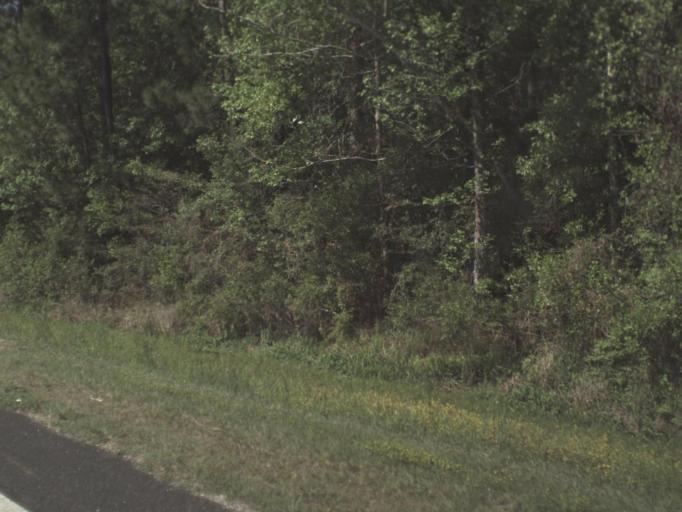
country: US
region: Florida
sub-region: Escambia County
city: Cantonment
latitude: 30.6405
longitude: -87.3427
